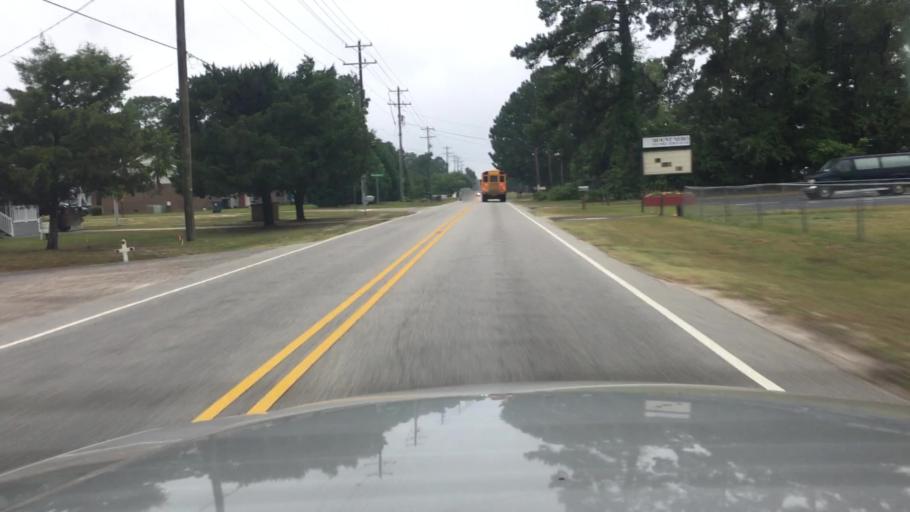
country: US
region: North Carolina
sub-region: Cumberland County
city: Hope Mills
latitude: 34.9756
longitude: -78.9733
